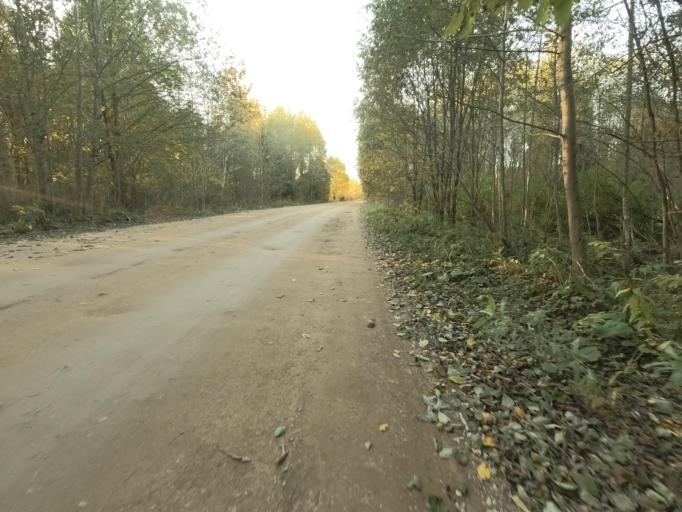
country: RU
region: Leningrad
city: Lyuban'
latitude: 58.9983
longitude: 31.1035
